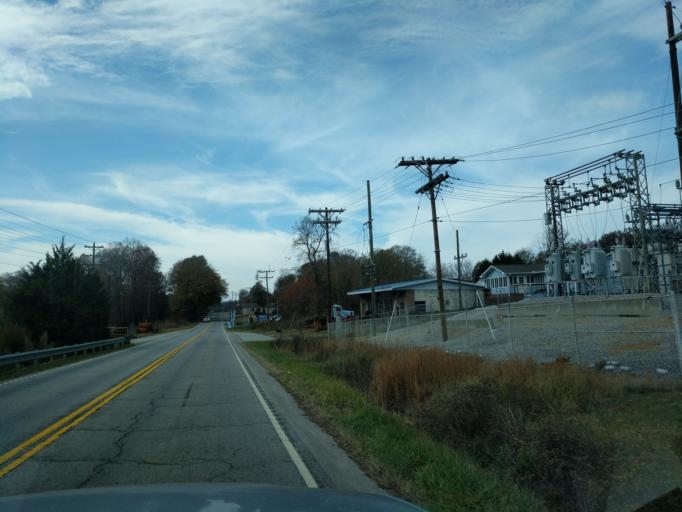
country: US
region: South Carolina
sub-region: Pickens County
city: Pickens
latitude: 34.8891
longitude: -82.6904
